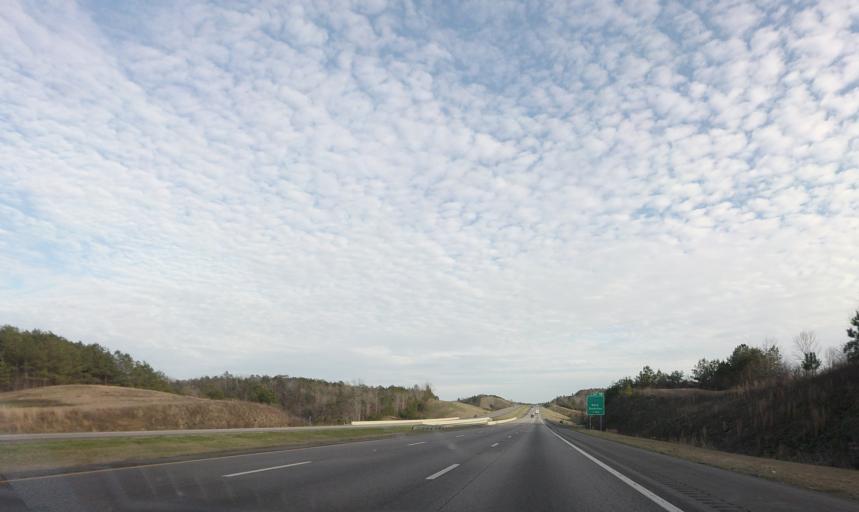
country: US
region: Alabama
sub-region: Walker County
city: Dora
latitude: 33.6860
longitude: -87.1056
